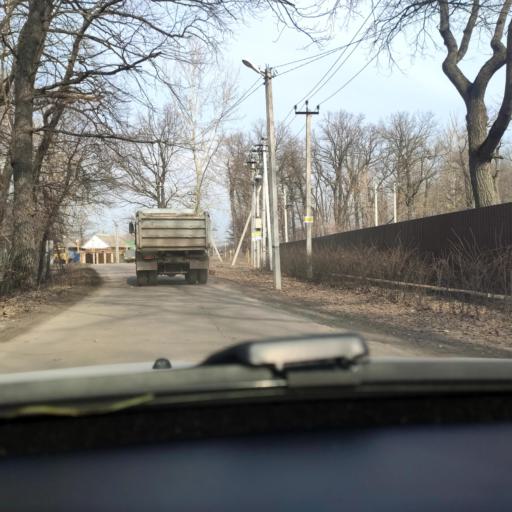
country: RU
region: Voronezj
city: Ramon'
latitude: 51.9026
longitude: 39.3652
